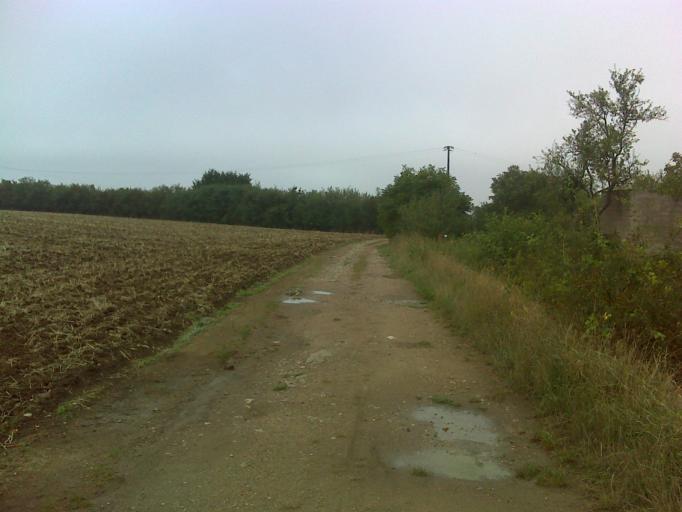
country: FR
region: Lorraine
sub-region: Departement de Meurthe-et-Moselle
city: Damelevieres
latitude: 48.5480
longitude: 6.3939
